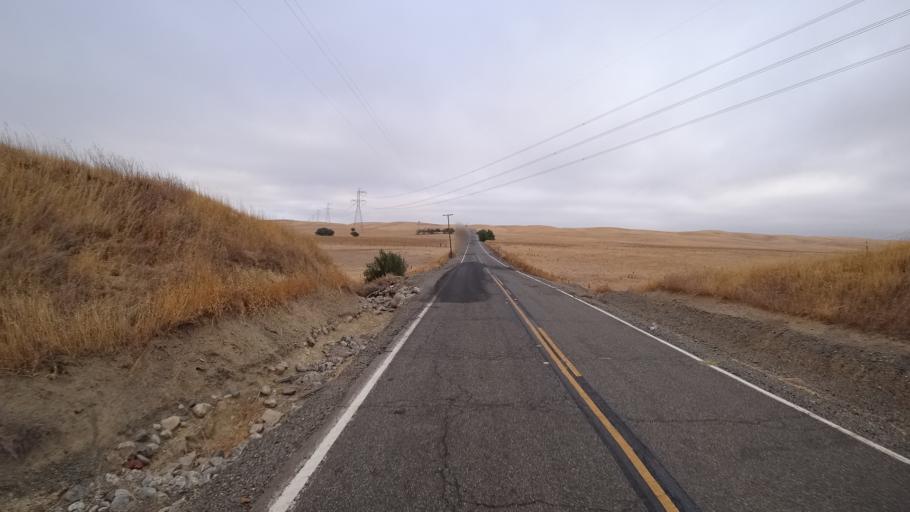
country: US
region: California
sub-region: Yolo County
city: Dunnigan
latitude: 38.8452
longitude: -122.0438
